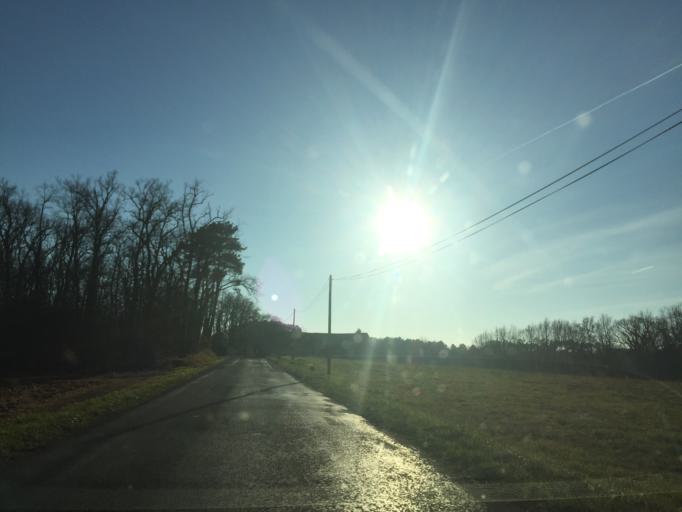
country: FR
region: Aquitaine
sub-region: Departement de la Dordogne
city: Riberac
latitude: 45.2027
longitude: 0.3454
